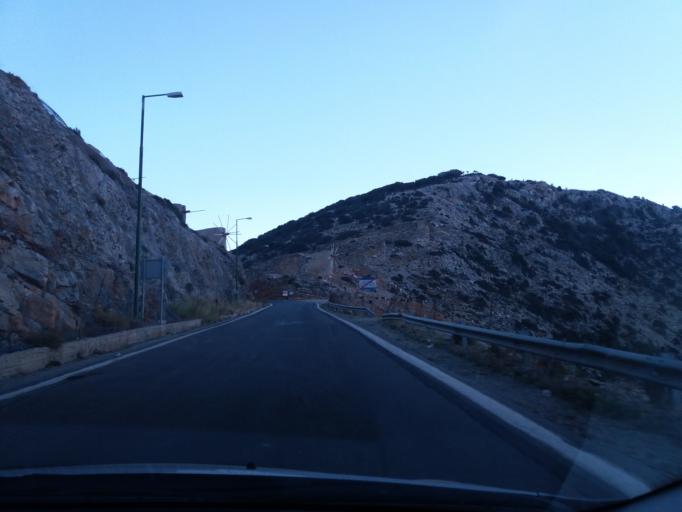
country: GR
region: Crete
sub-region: Nomos Irakleiou
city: Mokhos
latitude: 35.2053
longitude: 25.4547
